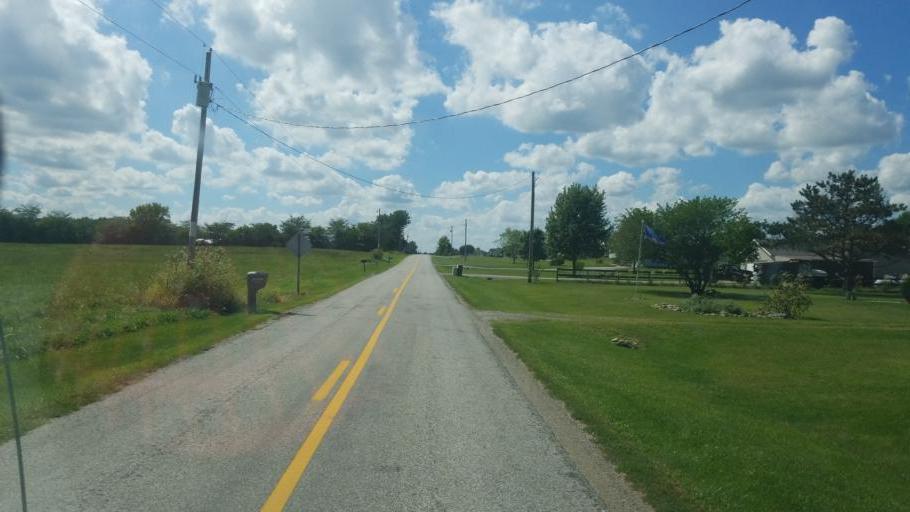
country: US
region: Ohio
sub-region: Marion County
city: Prospect
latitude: 40.3498
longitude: -83.1846
